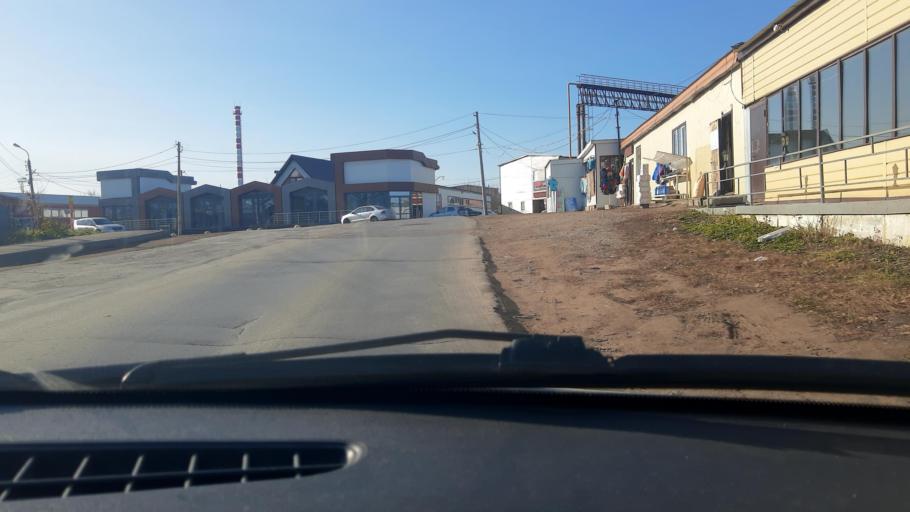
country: RU
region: Bashkortostan
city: Mikhaylovka
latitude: 54.7004
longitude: 55.8498
